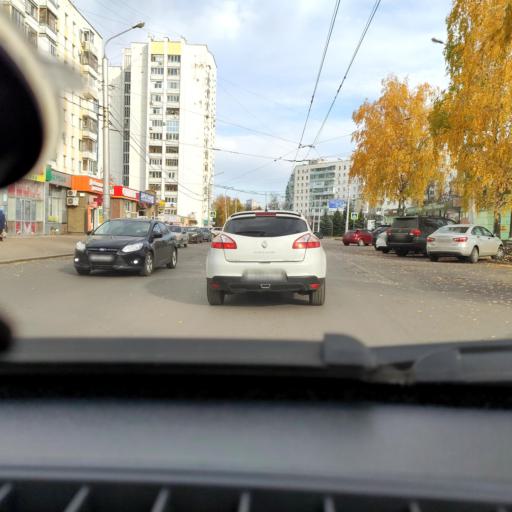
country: RU
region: Bashkortostan
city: Ufa
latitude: 54.7434
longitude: 56.0262
